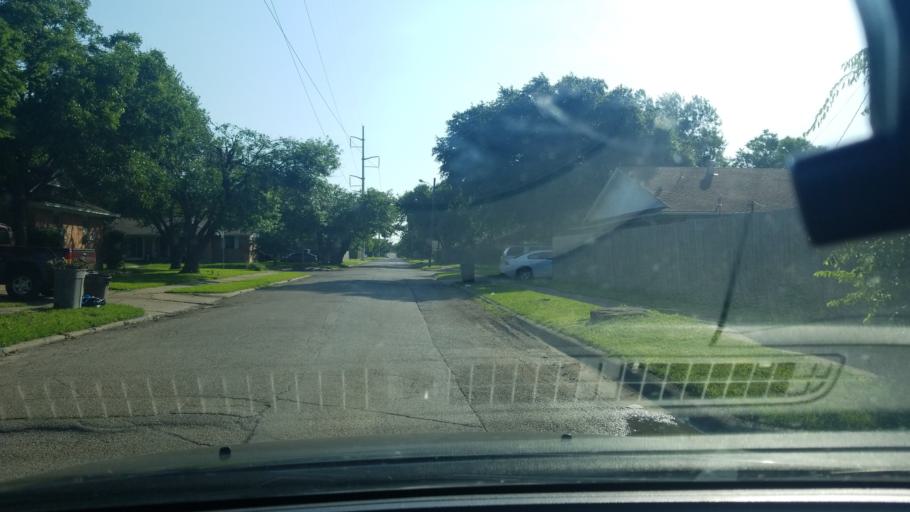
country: US
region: Texas
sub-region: Dallas County
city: Mesquite
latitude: 32.8232
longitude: -96.6434
